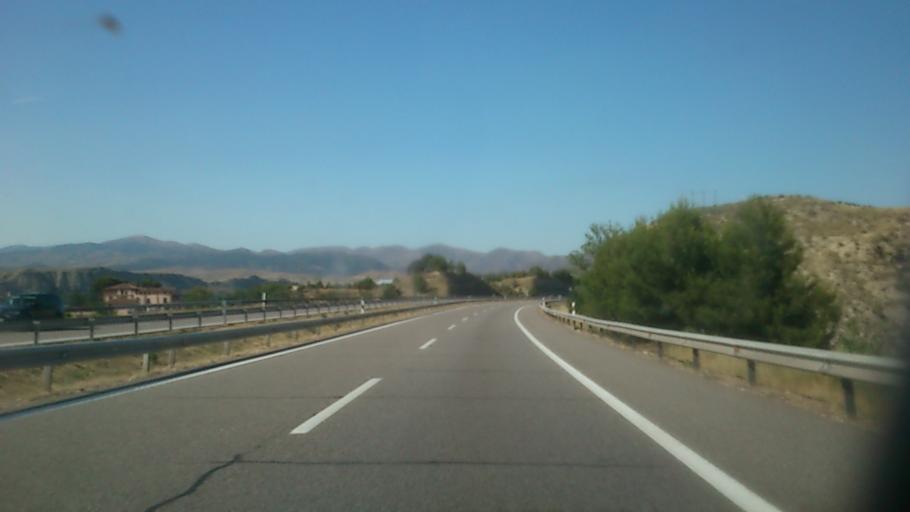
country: ES
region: Aragon
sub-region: Provincia de Zaragoza
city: Calatayud
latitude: 41.3425
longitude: -1.6306
